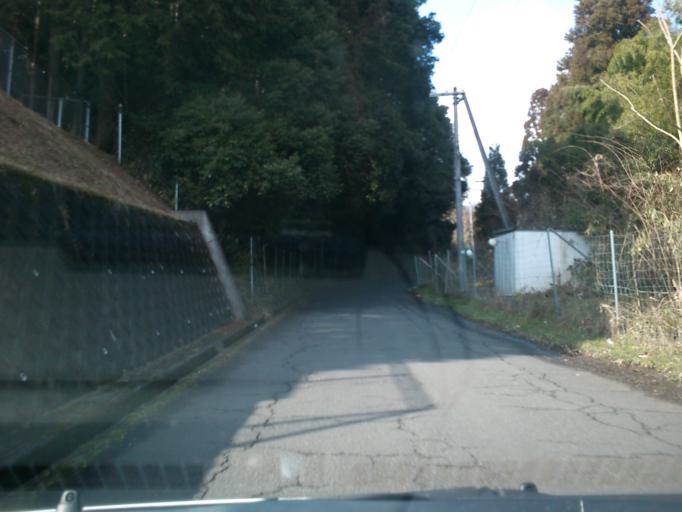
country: JP
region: Kyoto
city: Miyazu
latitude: 35.5806
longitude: 135.1776
